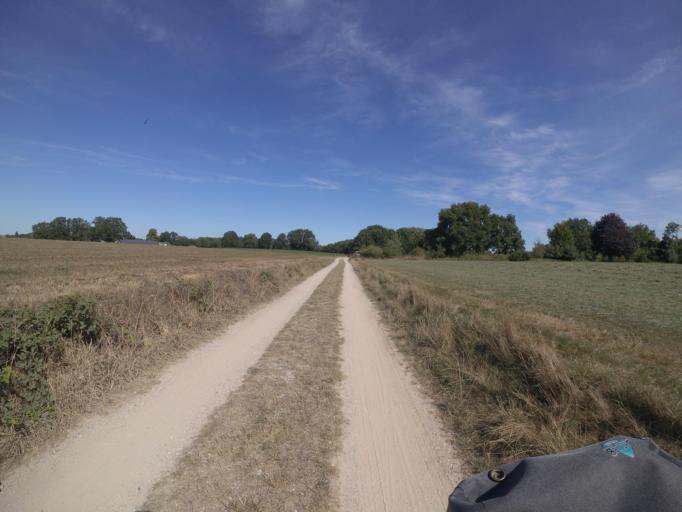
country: NL
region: Overijssel
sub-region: Gemeente Raalte
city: Raalte
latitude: 52.3620
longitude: 6.3989
